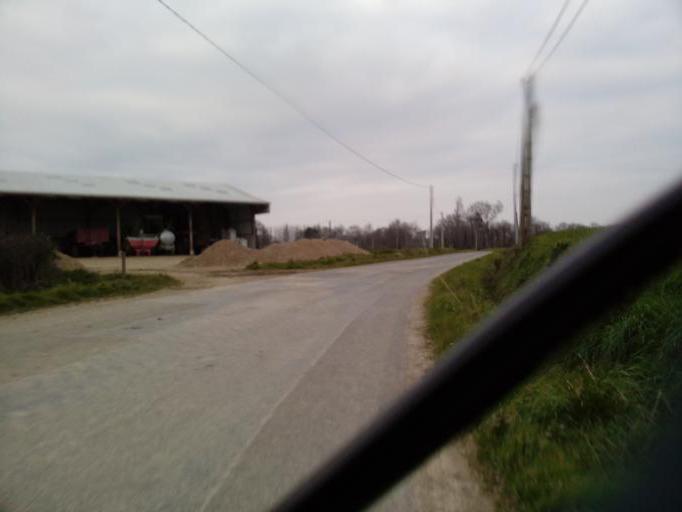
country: FR
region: Brittany
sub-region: Departement d'Ille-et-Vilaine
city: Cintre
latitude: 48.1038
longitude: -1.8950
